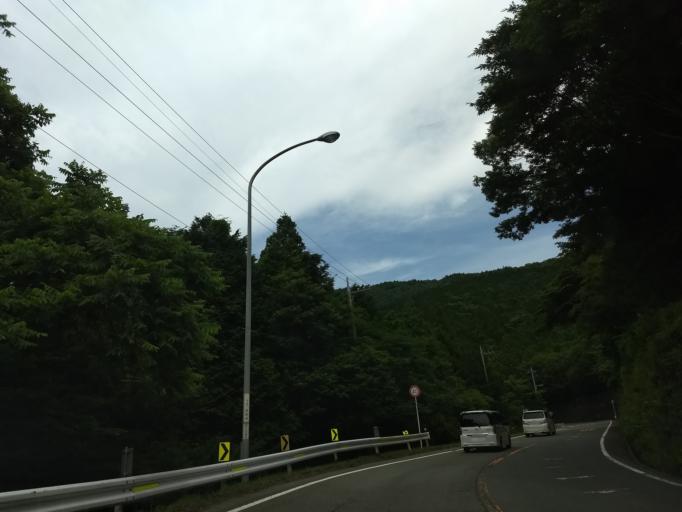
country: JP
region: Shizuoka
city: Gotemba
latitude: 35.3812
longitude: 138.8543
